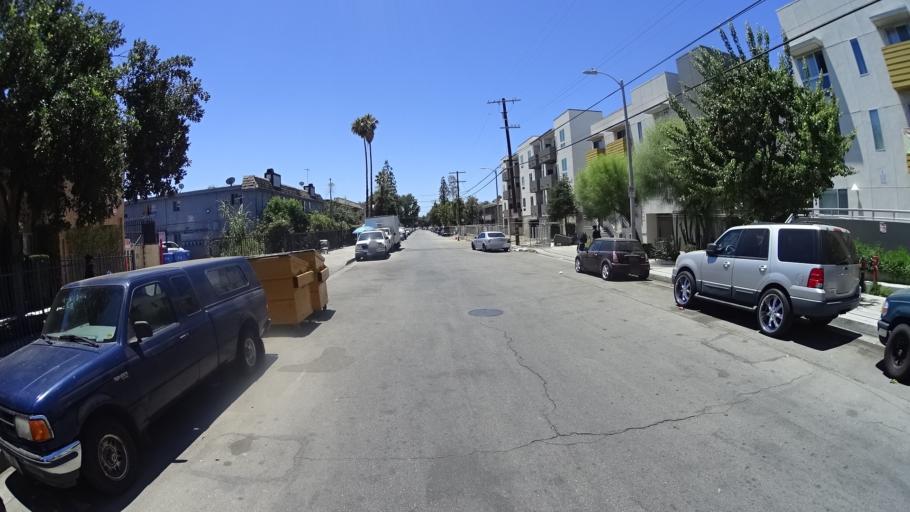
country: US
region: California
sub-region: Los Angeles County
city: Van Nuys
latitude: 34.2335
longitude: -118.4720
